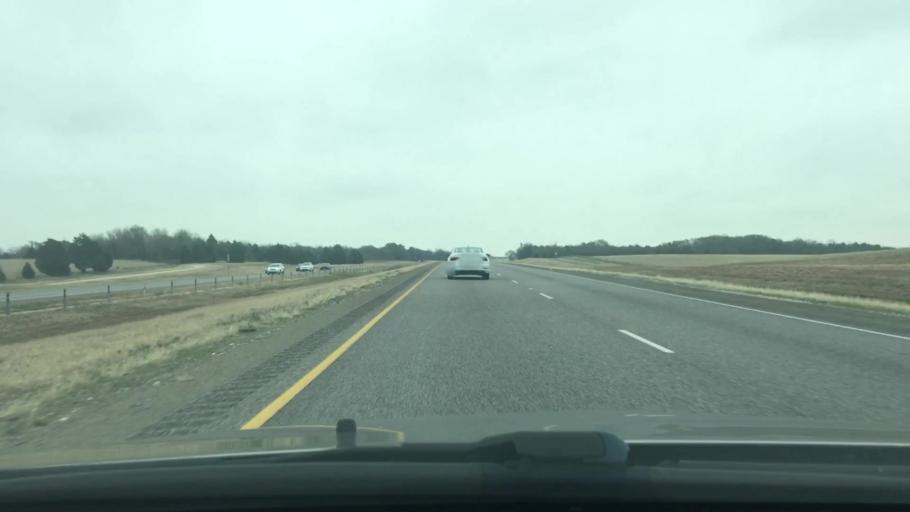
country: US
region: Texas
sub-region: Freestone County
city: Fairfield
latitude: 31.7835
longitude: -96.2372
